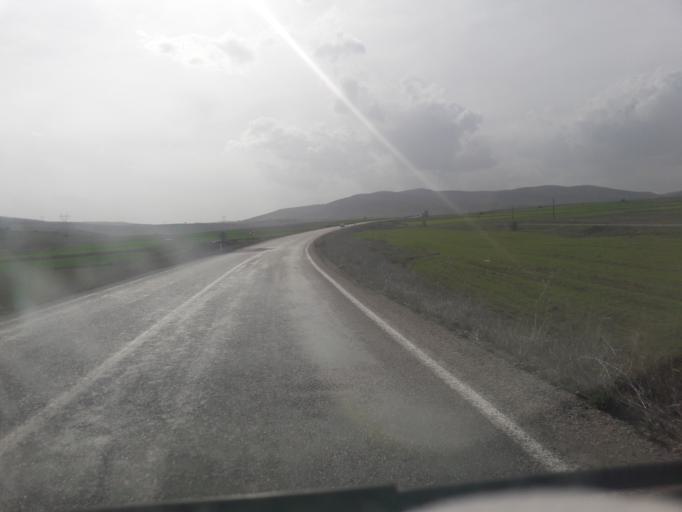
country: TR
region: Gumushane
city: Kelkit
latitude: 40.1253
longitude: 39.3406
